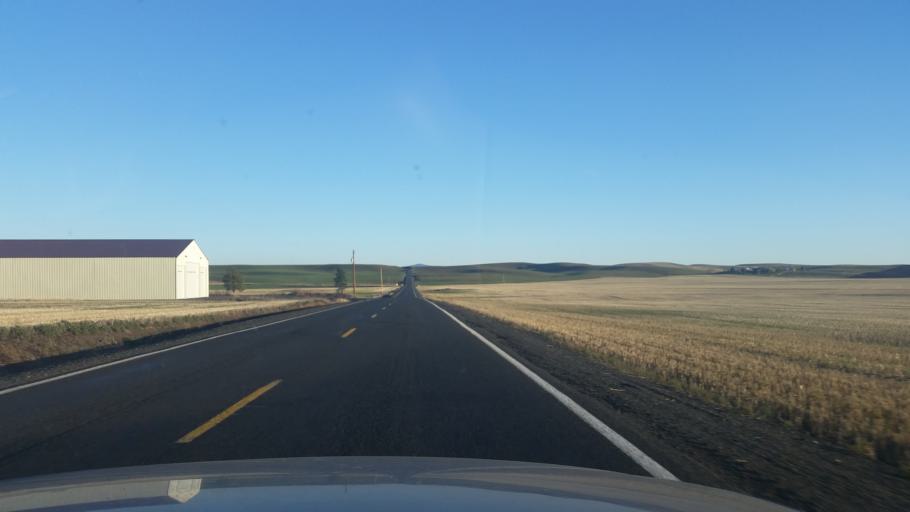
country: US
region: Washington
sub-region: Spokane County
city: Opportunity
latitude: 47.3658
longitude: -117.2890
